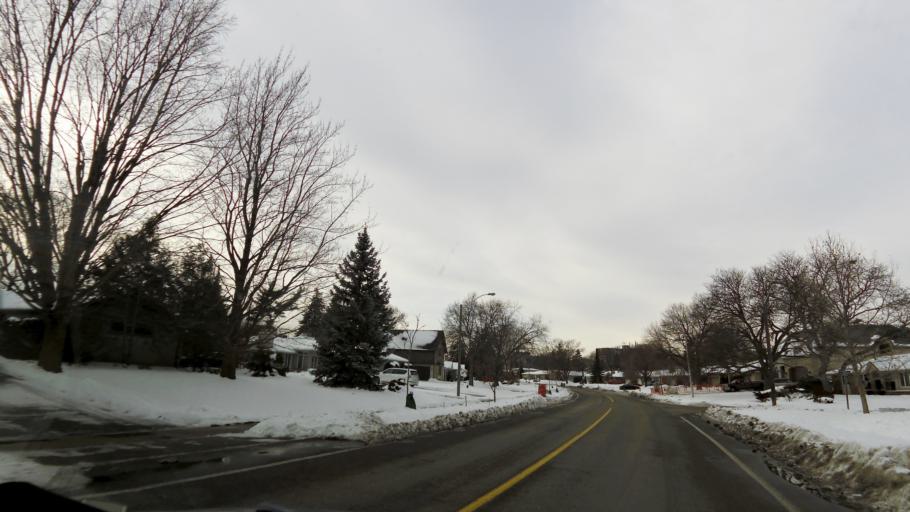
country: CA
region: Ontario
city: Etobicoke
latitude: 43.6734
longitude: -79.5454
